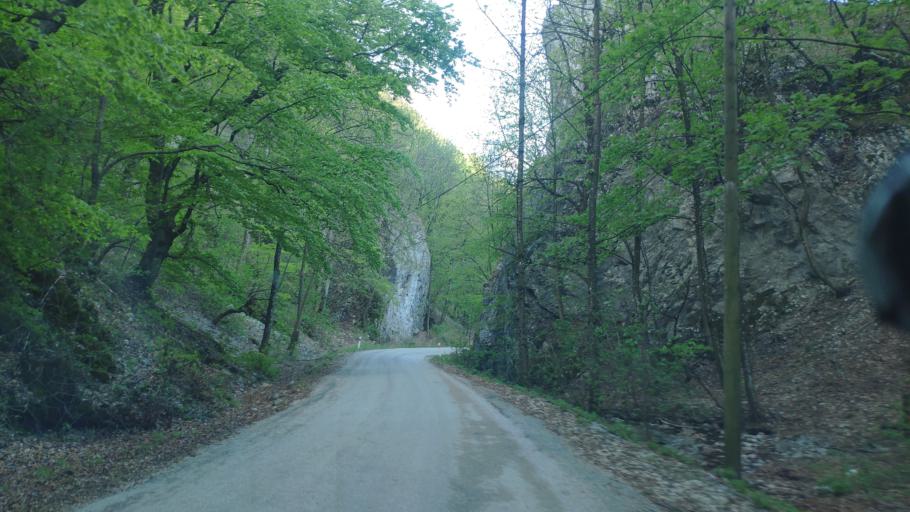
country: SK
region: Kosicky
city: Medzev
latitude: 48.6472
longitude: 20.8468
